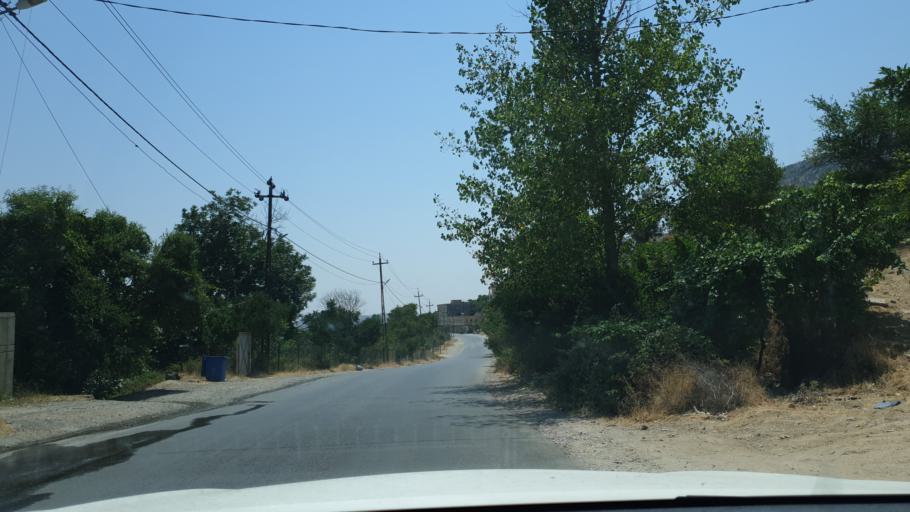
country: IQ
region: Arbil
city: Nahiyat Hiran
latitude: 36.2855
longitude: 44.4878
